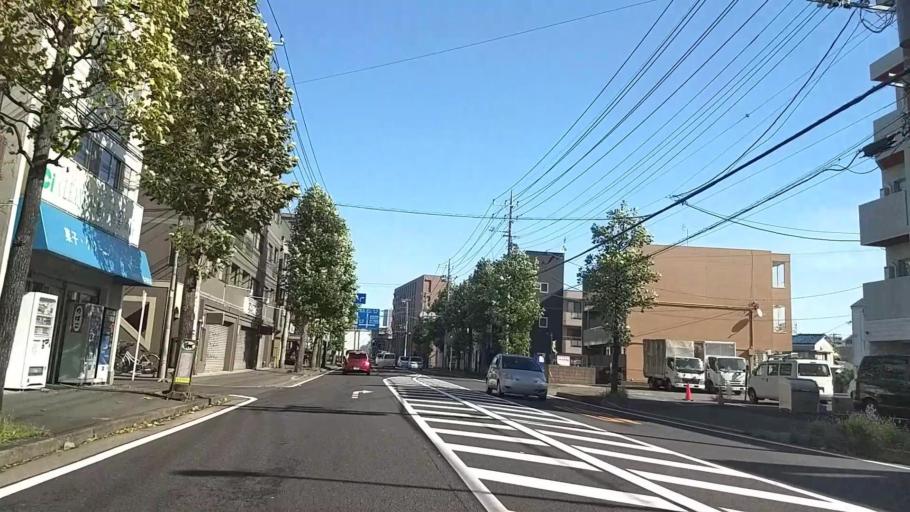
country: JP
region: Kanagawa
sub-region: Kawasaki-shi
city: Kawasaki
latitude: 35.5508
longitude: 139.6592
